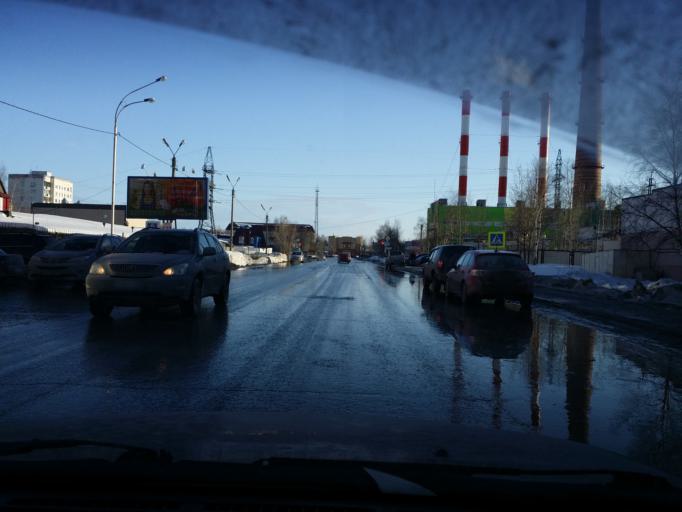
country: RU
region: Khanty-Mansiyskiy Avtonomnyy Okrug
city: Nizhnevartovsk
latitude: 60.9348
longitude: 76.5490
